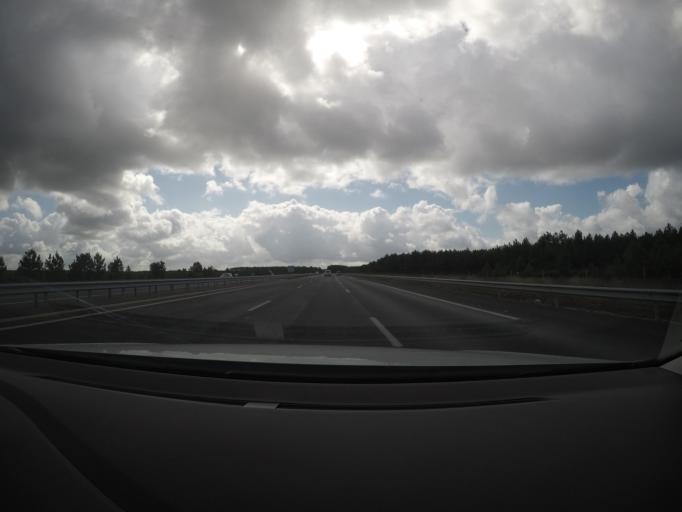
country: FR
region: Aquitaine
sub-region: Departement des Landes
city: Onesse-Laharie
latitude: 44.0628
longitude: -1.0056
